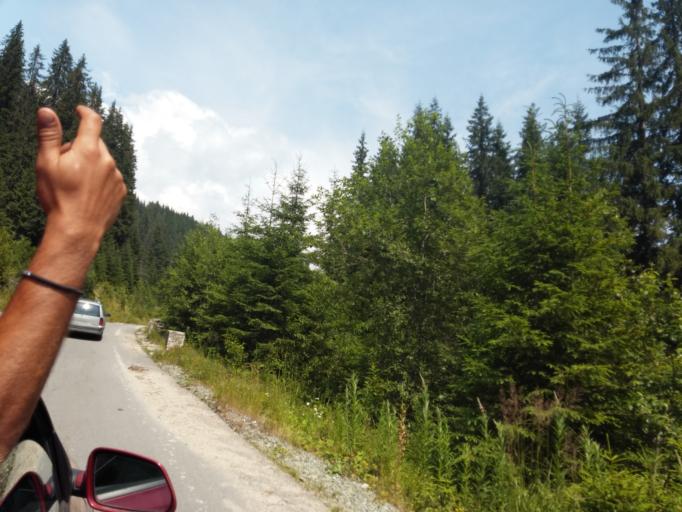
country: RO
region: Valcea
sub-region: Comuna Voineasa
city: Voineasa
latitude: 45.4256
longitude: 23.7816
